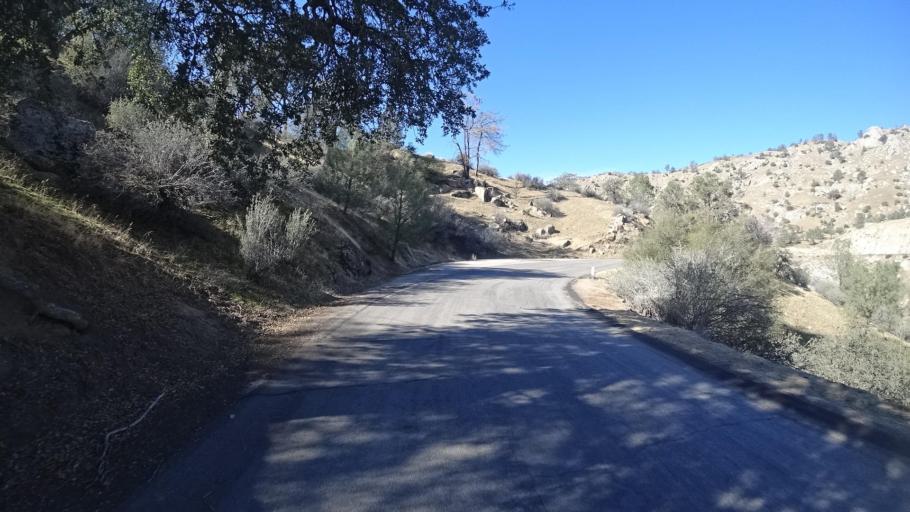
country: US
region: California
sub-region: Kern County
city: Bodfish
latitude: 35.5788
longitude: -118.5381
